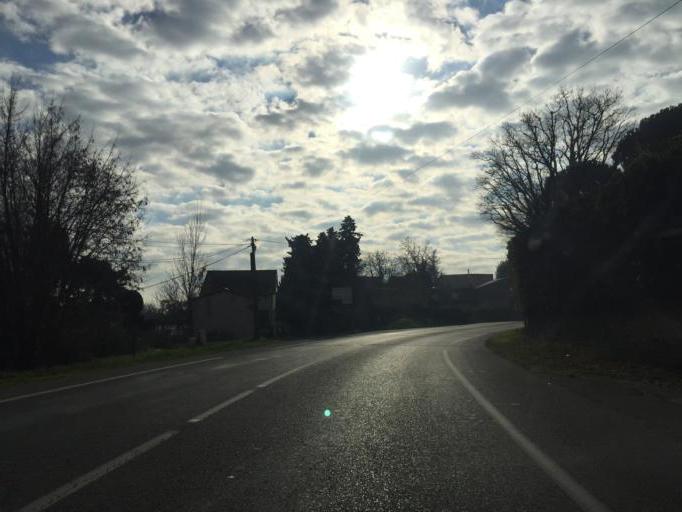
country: FR
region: Provence-Alpes-Cote d'Azur
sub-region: Departement du Vaucluse
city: Sarrians
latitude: 44.0890
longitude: 4.9714
